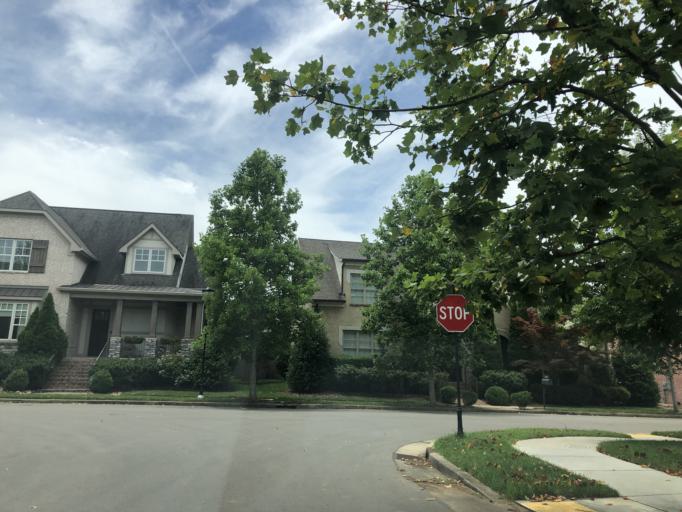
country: US
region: Tennessee
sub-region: Davidson County
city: Oak Hill
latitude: 36.1070
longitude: -86.8068
